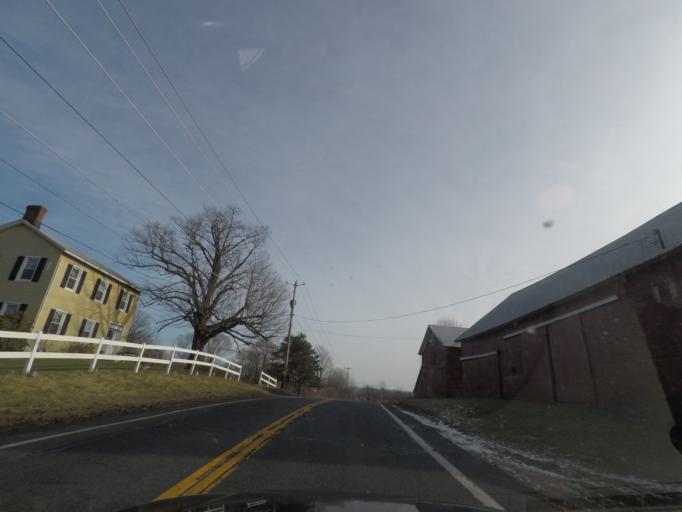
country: US
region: New York
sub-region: Saratoga County
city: Stillwater
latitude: 42.9848
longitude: -73.6713
